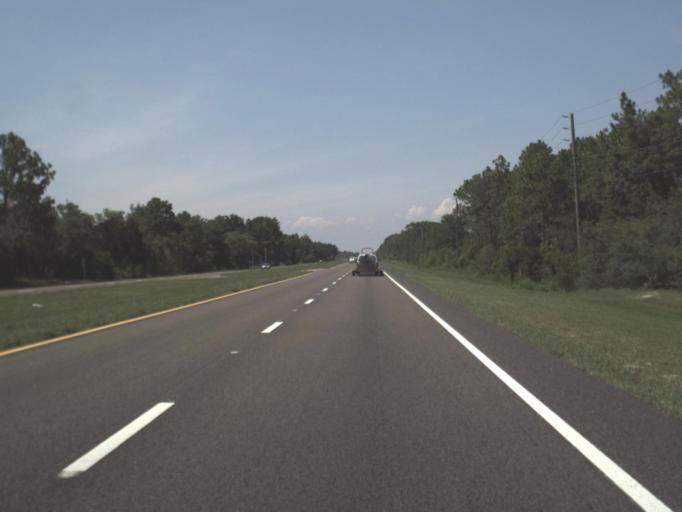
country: US
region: Florida
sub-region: Citrus County
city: Sugarmill Woods
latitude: 28.7110
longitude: -82.5525
